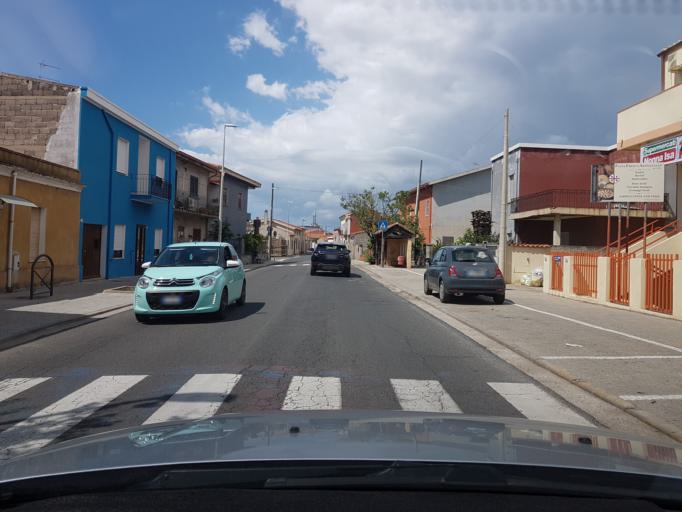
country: IT
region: Sardinia
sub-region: Provincia di Oristano
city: Riola Sardo
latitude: 39.9929
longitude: 8.5416
